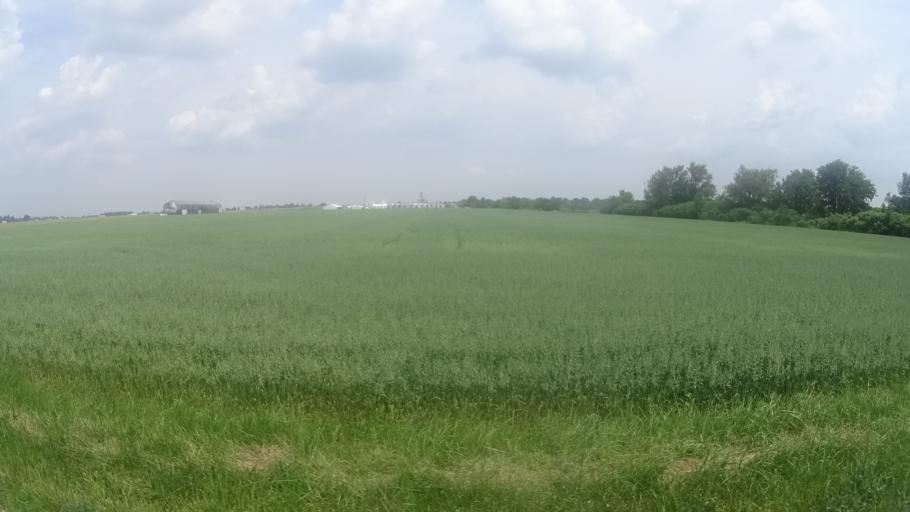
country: US
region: Ohio
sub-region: Huron County
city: Monroeville
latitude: 41.3235
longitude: -82.7000
